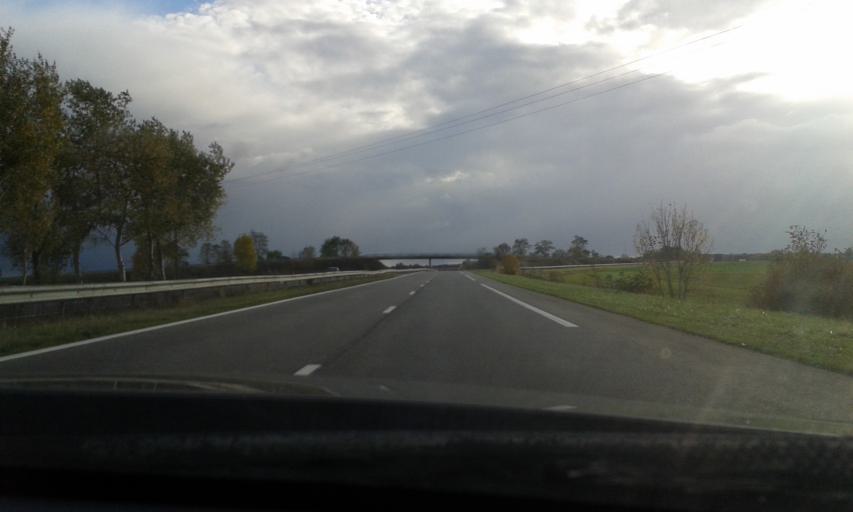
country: FR
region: Haute-Normandie
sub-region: Departement de l'Eure
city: Normanville
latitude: 49.0890
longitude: 1.1884
